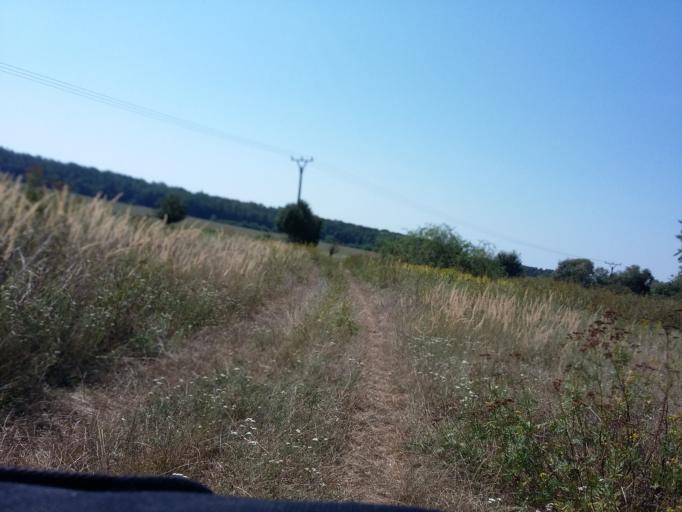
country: SK
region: Bratislavsky
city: Stupava
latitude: 48.3254
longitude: 17.0398
